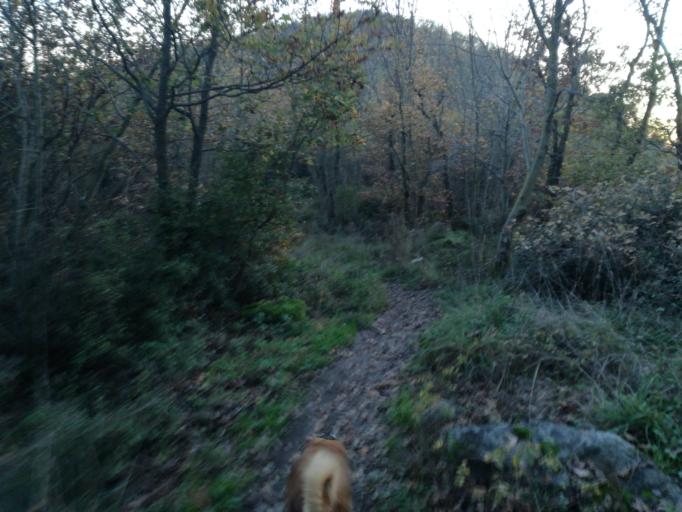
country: IT
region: Veneto
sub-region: Provincia di Padova
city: Battaglia Terme
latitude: 45.3037
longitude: 11.7683
